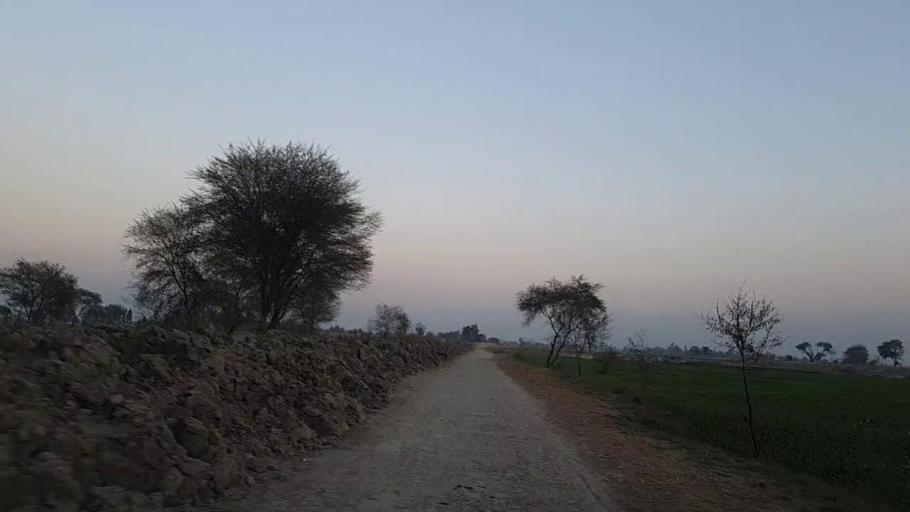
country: PK
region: Sindh
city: Naushahro Firoz
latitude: 26.7947
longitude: 68.0385
